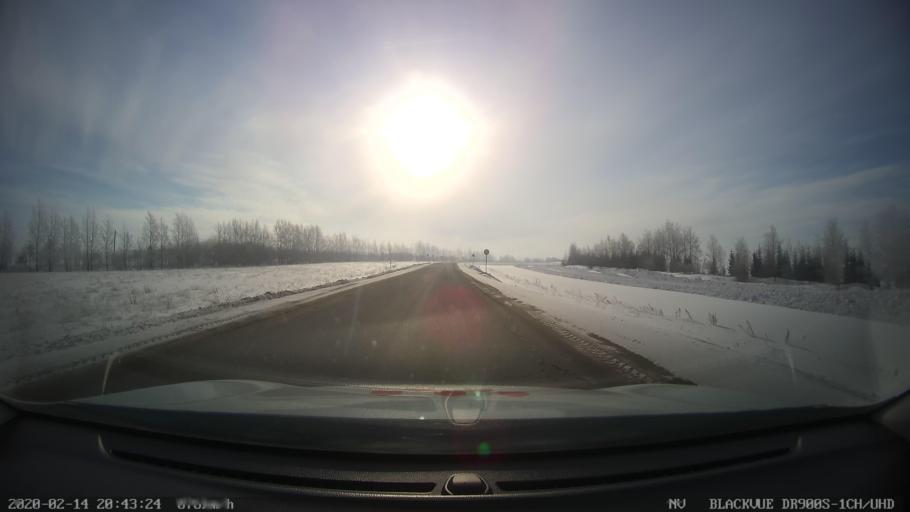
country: RU
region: Tatarstan
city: Kuybyshevskiy Zaton
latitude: 55.3084
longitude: 49.1476
